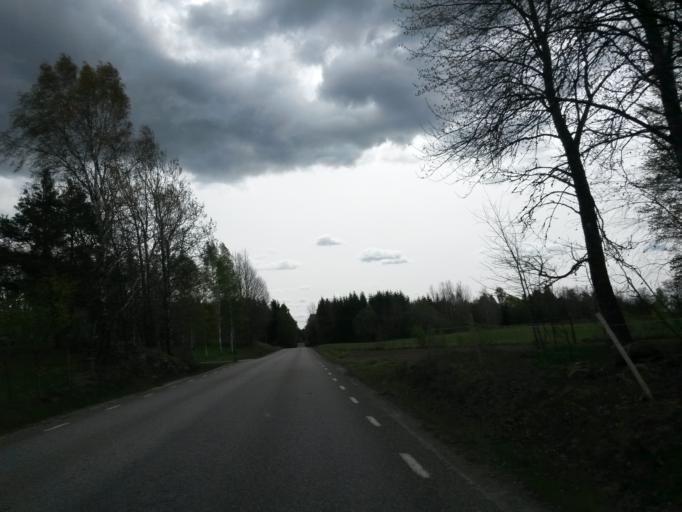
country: SE
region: Vaestra Goetaland
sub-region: Herrljunga Kommun
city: Herrljunga
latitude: 58.1470
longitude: 13.0203
